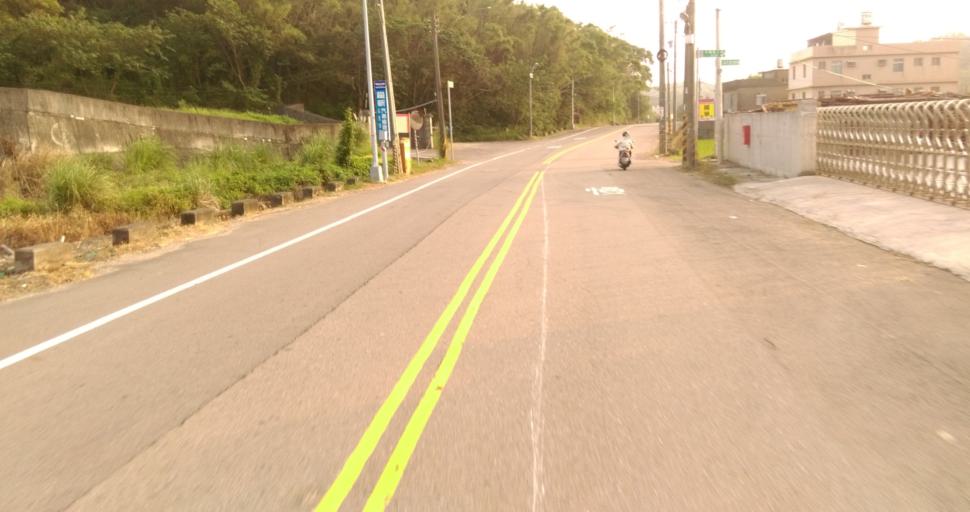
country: TW
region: Taiwan
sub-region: Hsinchu
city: Hsinchu
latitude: 24.7509
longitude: 120.9381
